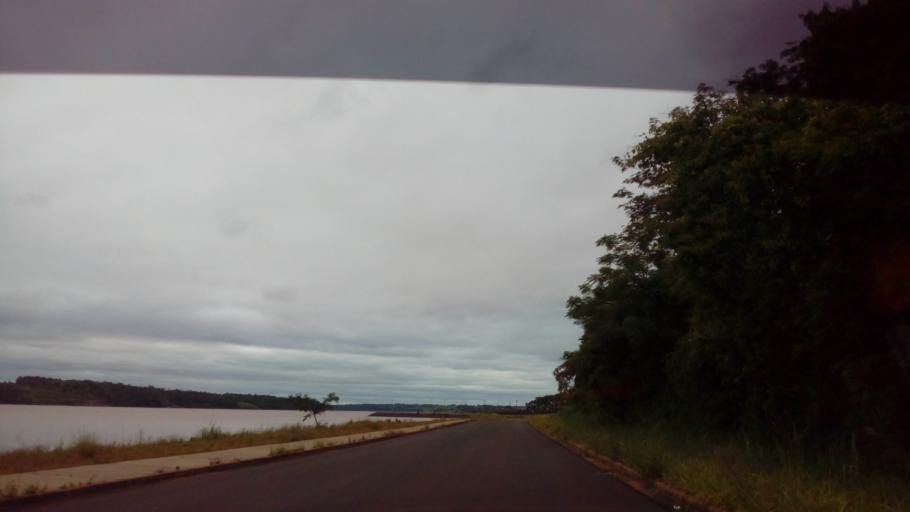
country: AR
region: Misiones
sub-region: Departamento de Candelaria
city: Candelaria
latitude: -27.4508
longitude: -55.7584
